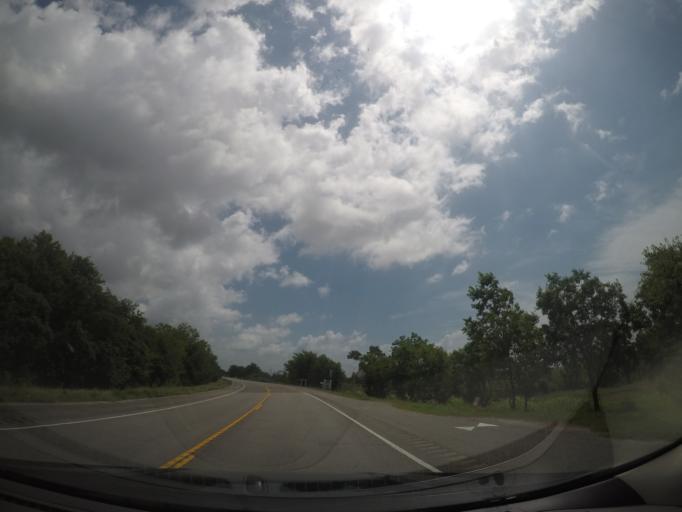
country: US
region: Louisiana
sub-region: Saint Tammany Parish
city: Eden Isle
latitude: 30.0939
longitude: -89.7682
